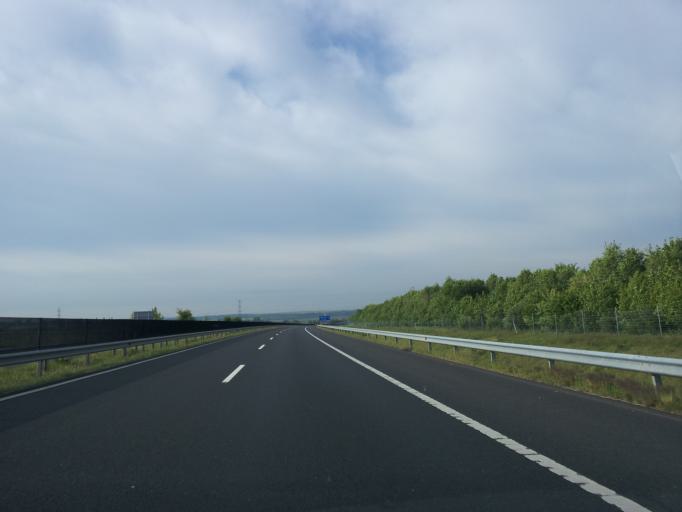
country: HU
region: Fejer
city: Rackeresztur
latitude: 47.2760
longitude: 18.8607
